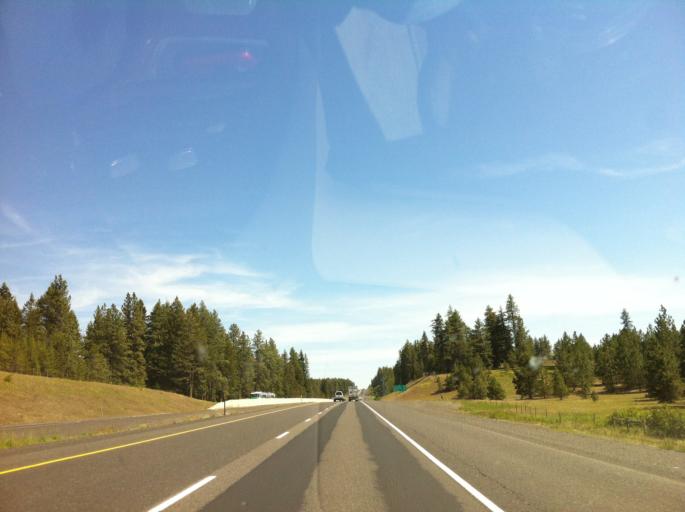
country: US
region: Oregon
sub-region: Umatilla County
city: Mission
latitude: 45.4999
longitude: -118.4203
